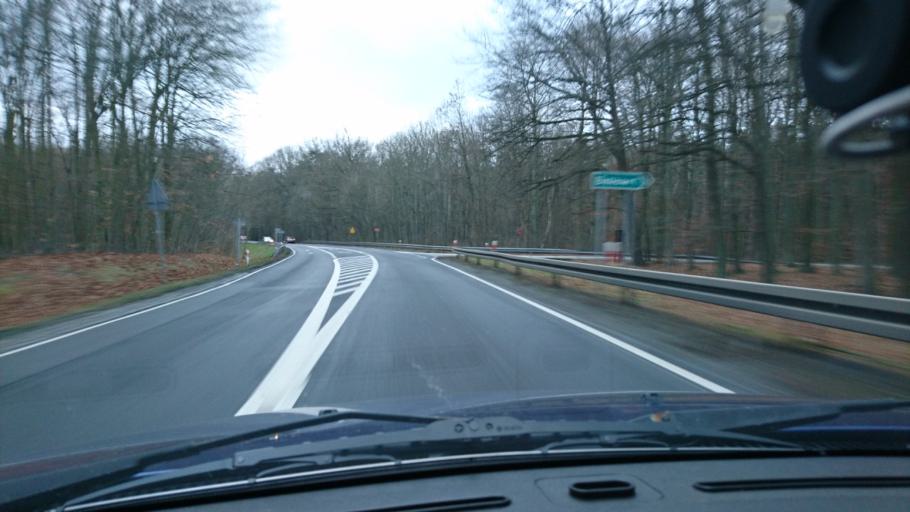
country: PL
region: Opole Voivodeship
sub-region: Powiat kluczborski
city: Kluczbork
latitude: 50.9606
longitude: 18.3010
